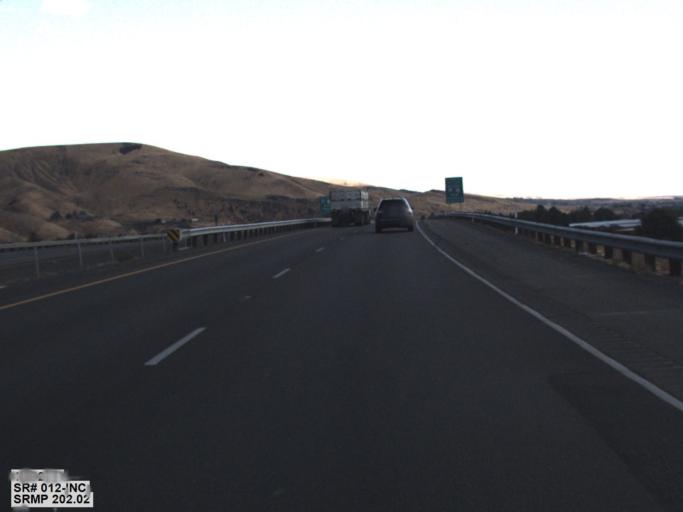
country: US
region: Washington
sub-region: Yakima County
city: Selah
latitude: 46.6260
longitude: -120.5227
